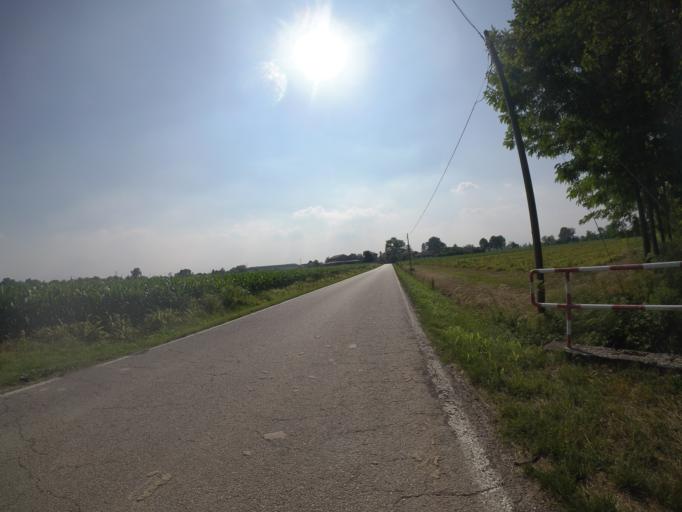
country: IT
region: Friuli Venezia Giulia
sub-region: Provincia di Udine
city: Camino al Tagliamento
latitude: 45.9194
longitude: 12.9742
